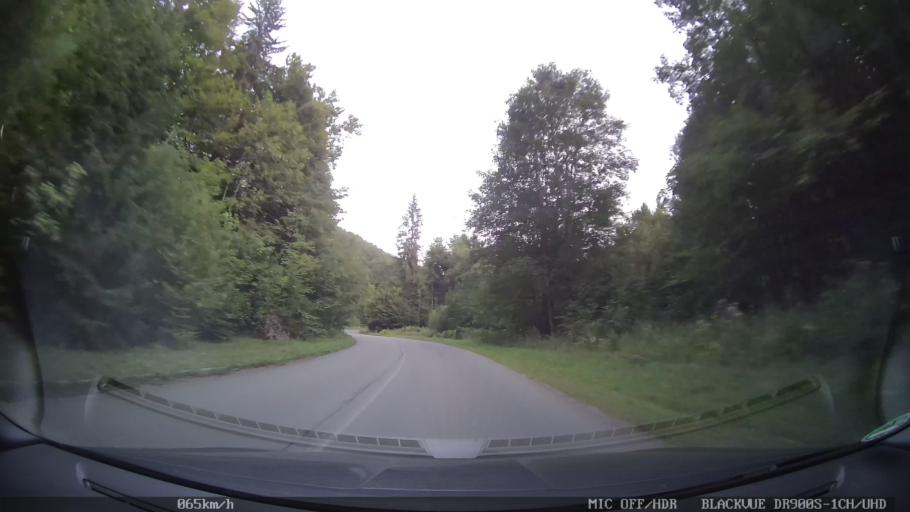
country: HR
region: Primorsko-Goranska
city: Vrbovsko
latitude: 45.2107
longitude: 15.0289
